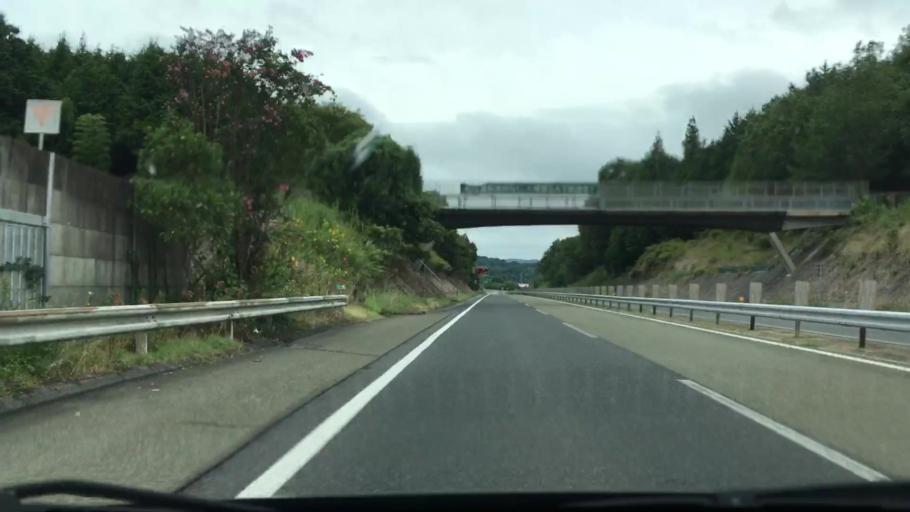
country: JP
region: Hiroshima
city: Shobara
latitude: 34.8441
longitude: 133.0319
